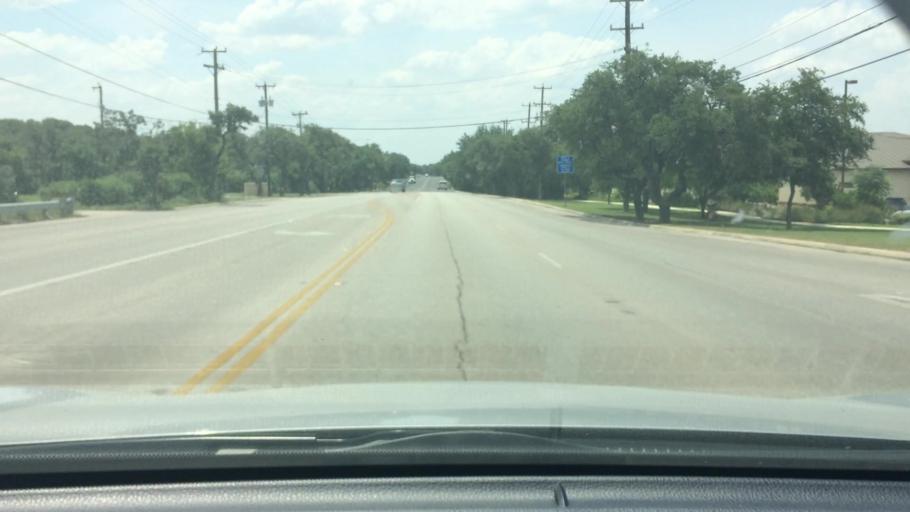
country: US
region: Texas
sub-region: Bexar County
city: Shavano Park
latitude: 29.5975
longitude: -98.5626
